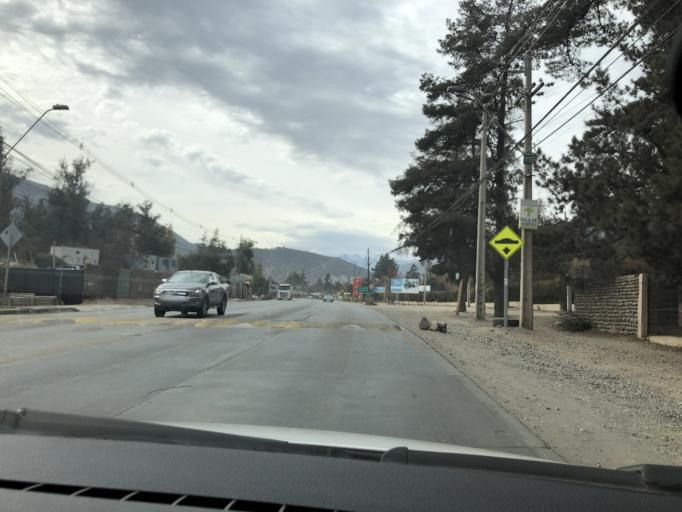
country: CL
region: Santiago Metropolitan
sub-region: Provincia de Cordillera
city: Puente Alto
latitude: -33.5988
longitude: -70.5277
